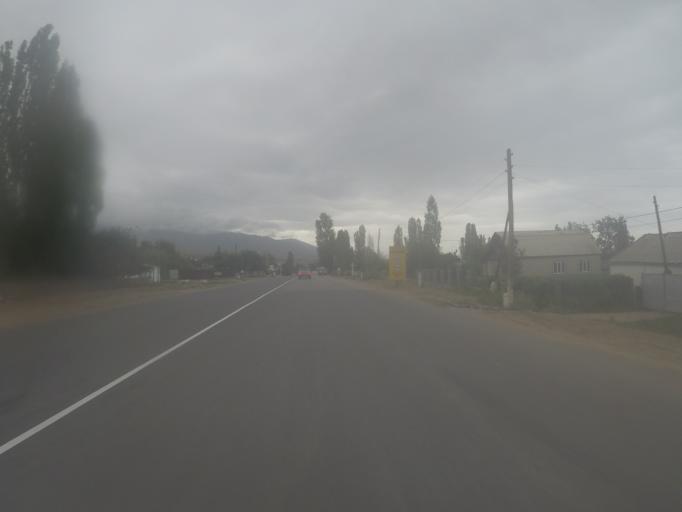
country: KG
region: Ysyk-Koel
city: Cholpon-Ata
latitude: 42.6706
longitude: 77.2926
